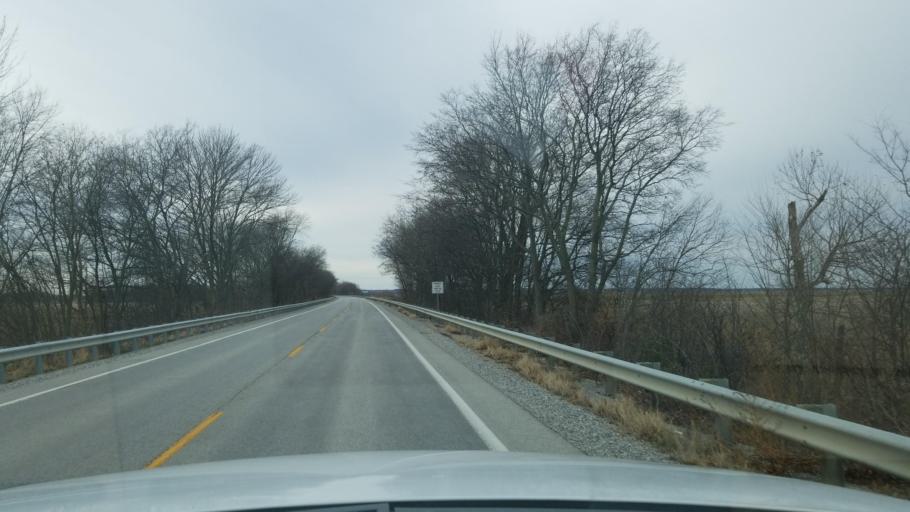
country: US
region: Indiana
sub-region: Posey County
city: Mount Vernon
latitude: 37.9434
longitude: -88.0496
